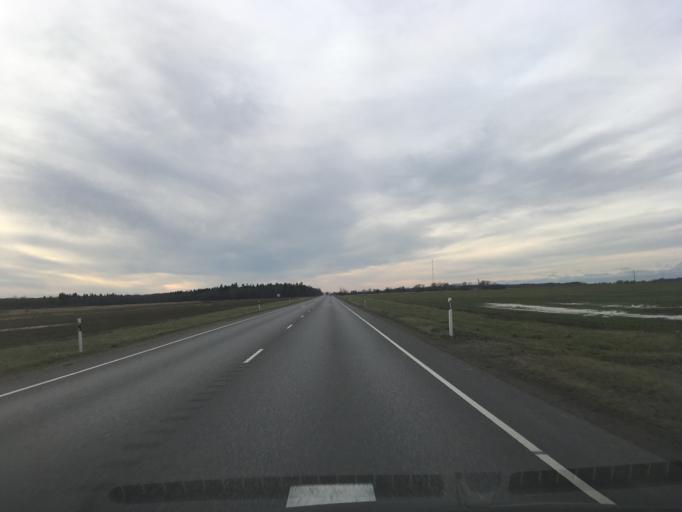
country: EE
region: Ida-Virumaa
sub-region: Kohtla-Jaerve linn
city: Kohtla-Jarve
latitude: 59.4209
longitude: 27.2341
